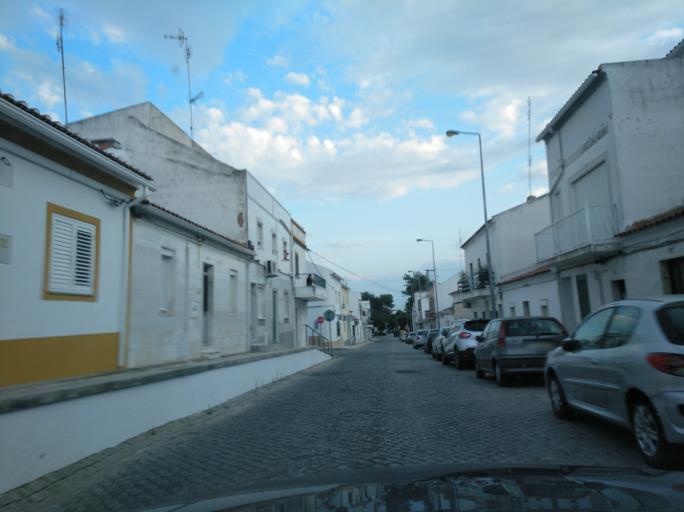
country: PT
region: Portalegre
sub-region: Campo Maior
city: Campo Maior
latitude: 39.0167
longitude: -7.0686
